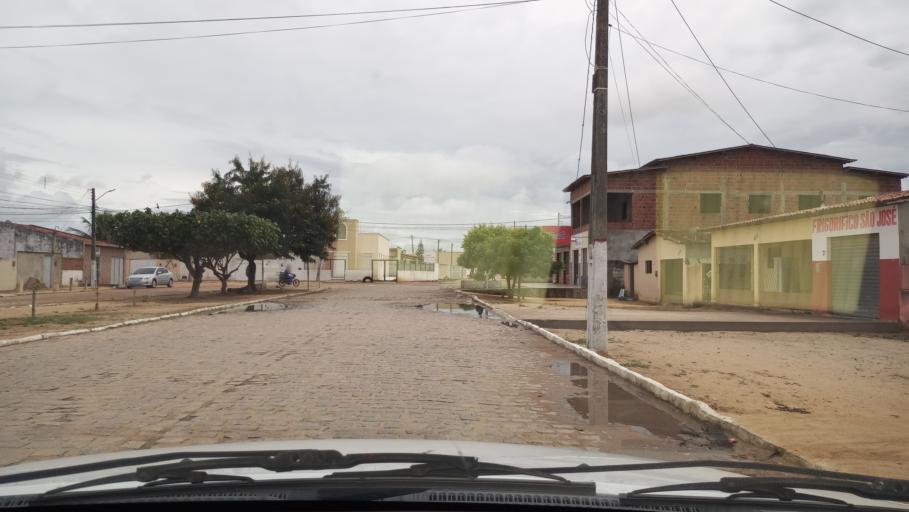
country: BR
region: Rio Grande do Norte
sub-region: Poco Branco
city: Poco Branco
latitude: -5.6205
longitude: -35.6660
